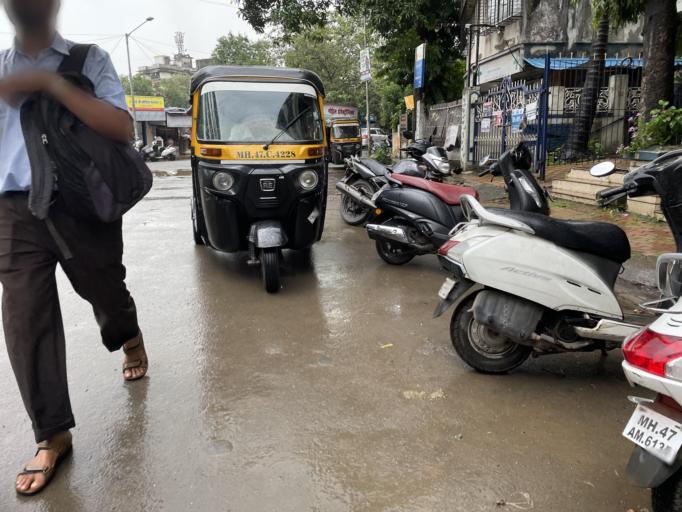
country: IN
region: Maharashtra
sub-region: Mumbai Suburban
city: Borivli
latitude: 19.2529
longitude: 72.8624
